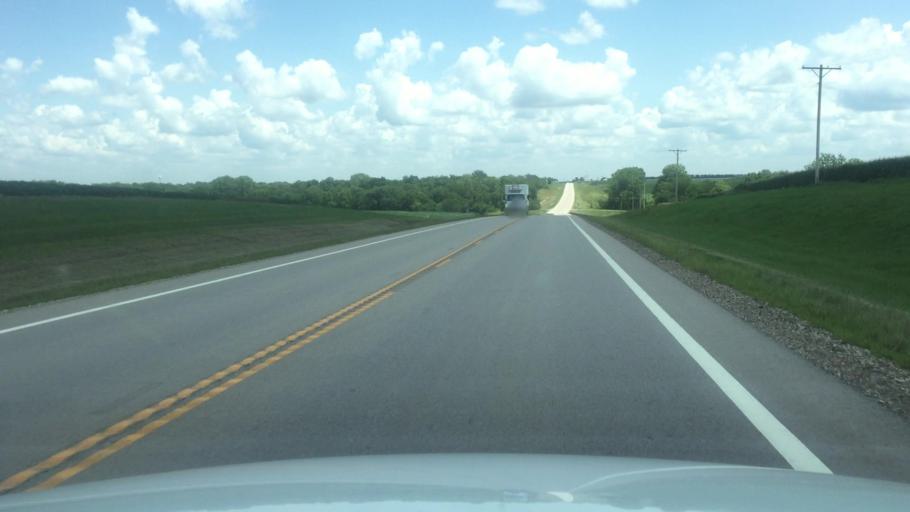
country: US
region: Kansas
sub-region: Brown County
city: Horton
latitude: 39.6673
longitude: -95.4574
